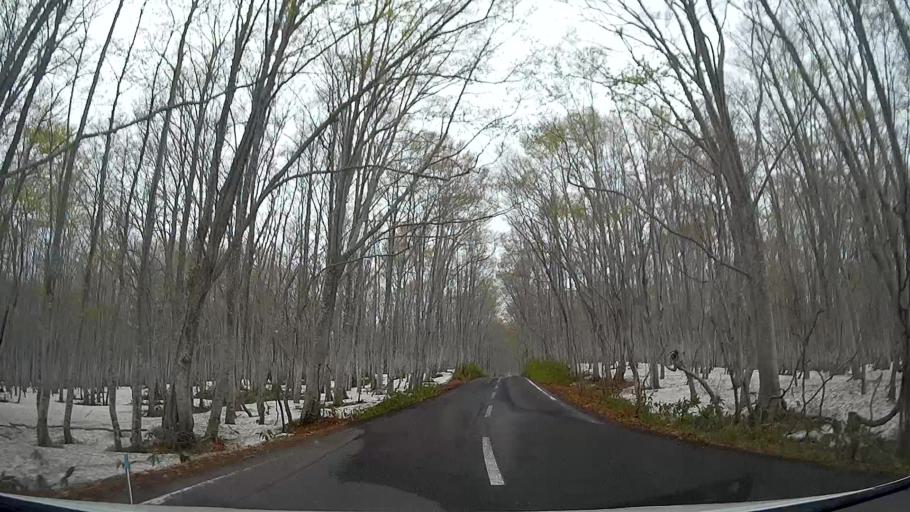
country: JP
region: Aomori
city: Aomori Shi
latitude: 40.6286
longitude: 140.9367
